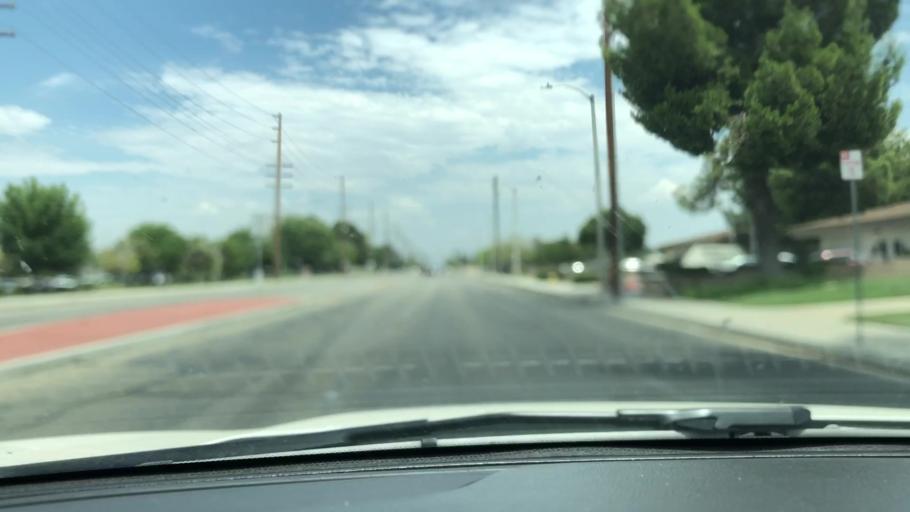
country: US
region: California
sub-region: Los Angeles County
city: Quartz Hill
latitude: 34.6748
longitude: -118.1871
